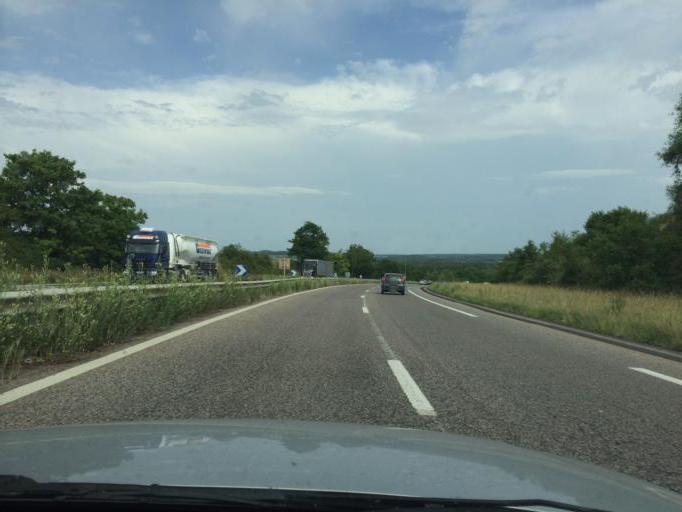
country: FR
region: Lorraine
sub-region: Departement de Meurthe-et-Moselle
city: Varangeville
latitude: 48.6167
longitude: 6.3215
